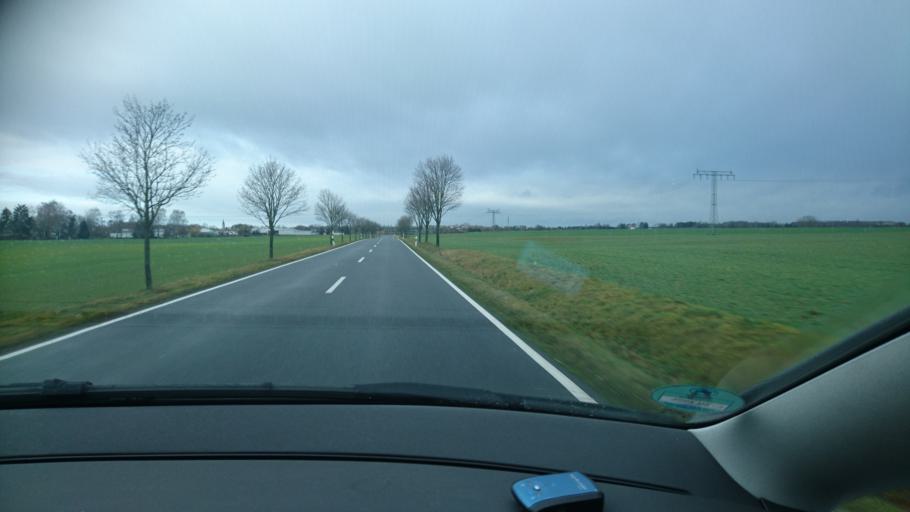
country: DE
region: Saxony
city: Bad Duben
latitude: 51.5876
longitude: 12.6147
